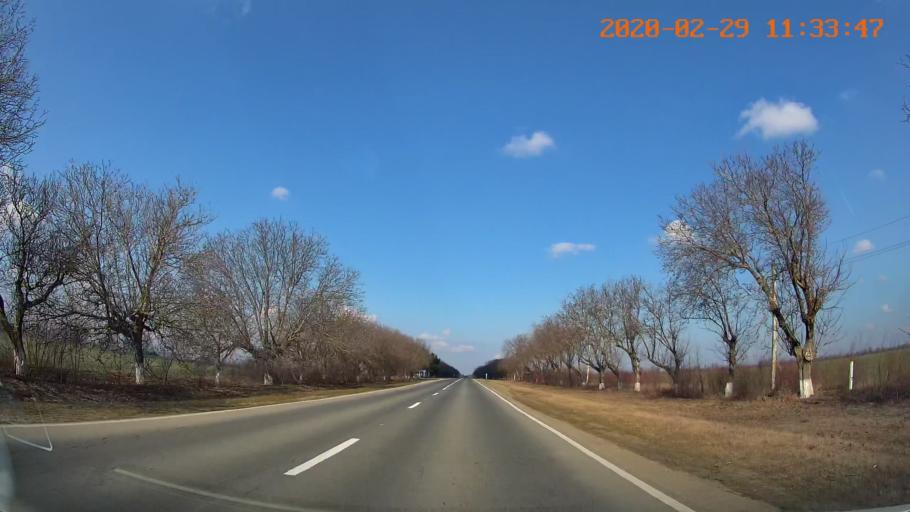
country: MD
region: Rezina
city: Saharna
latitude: 47.5564
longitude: 29.0808
